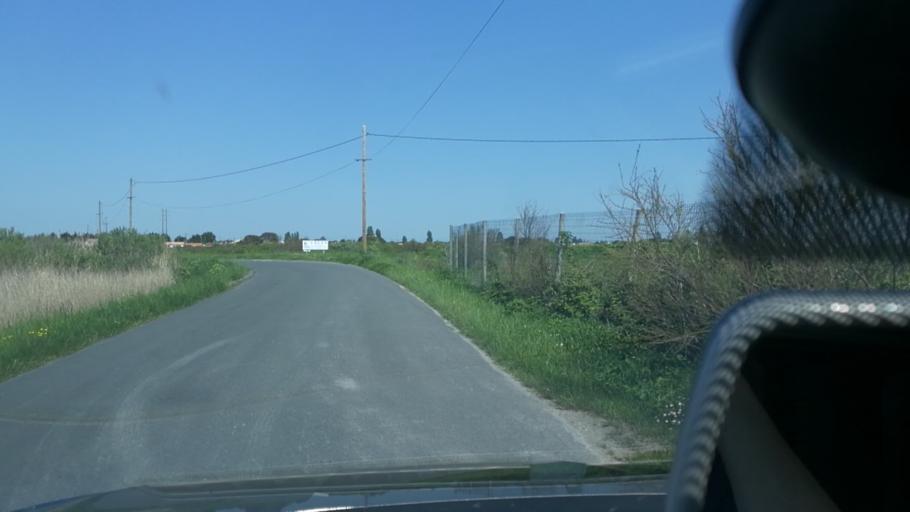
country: FR
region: Poitou-Charentes
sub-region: Departement de la Charente-Maritime
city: Saint-Trojan-les-Bains
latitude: 45.8667
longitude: -1.2208
